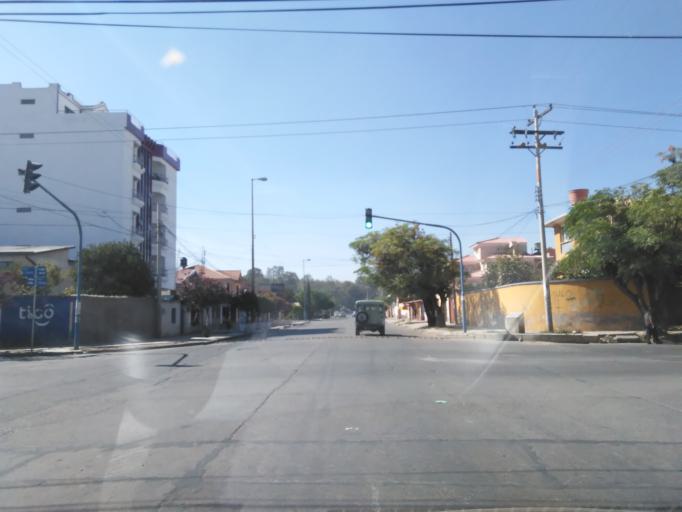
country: BO
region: Cochabamba
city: Cochabamba
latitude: -17.4002
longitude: -66.1794
